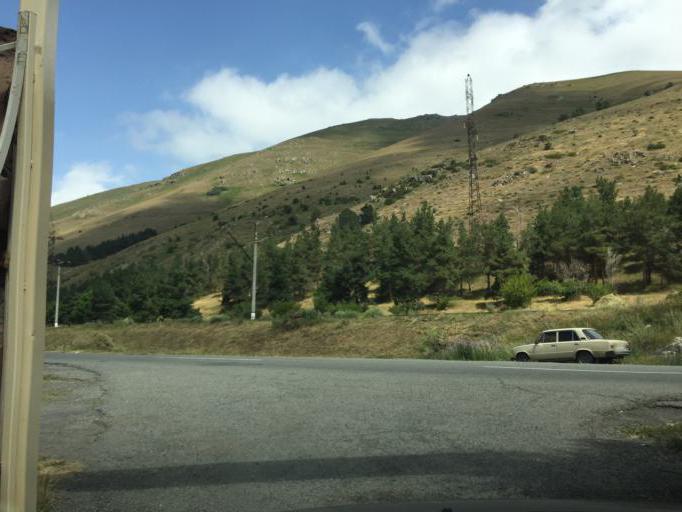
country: AM
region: Geghark'unik'i Marz
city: Tsovagyugh
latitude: 40.6227
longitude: 45.0151
